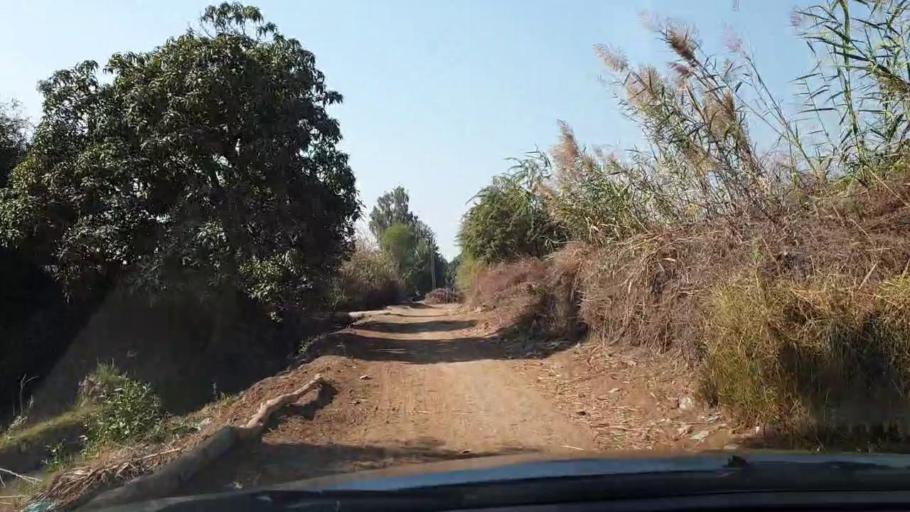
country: PK
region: Sindh
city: Jhol
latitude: 25.8983
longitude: 68.8961
